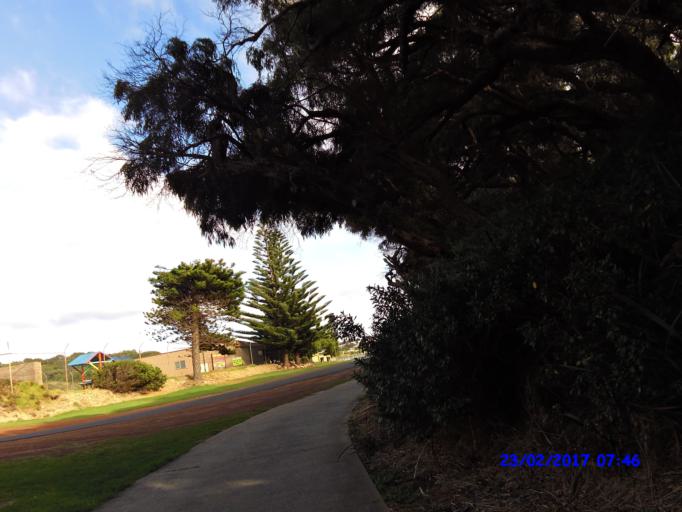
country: AU
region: Western Australia
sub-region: Augusta-Margaret River Shire
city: Augusta
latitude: -34.3253
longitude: 115.1700
